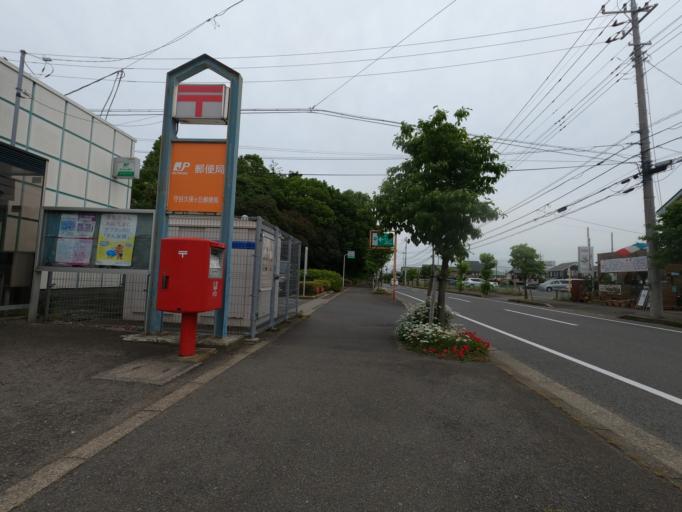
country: JP
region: Ibaraki
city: Moriya
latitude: 35.9675
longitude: 139.9767
